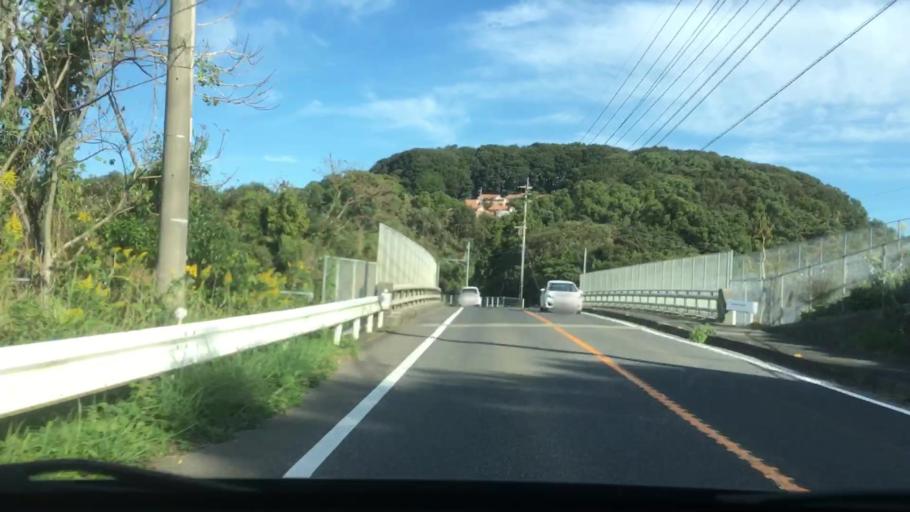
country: JP
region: Nagasaki
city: Sasebo
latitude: 33.0675
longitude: 129.7640
